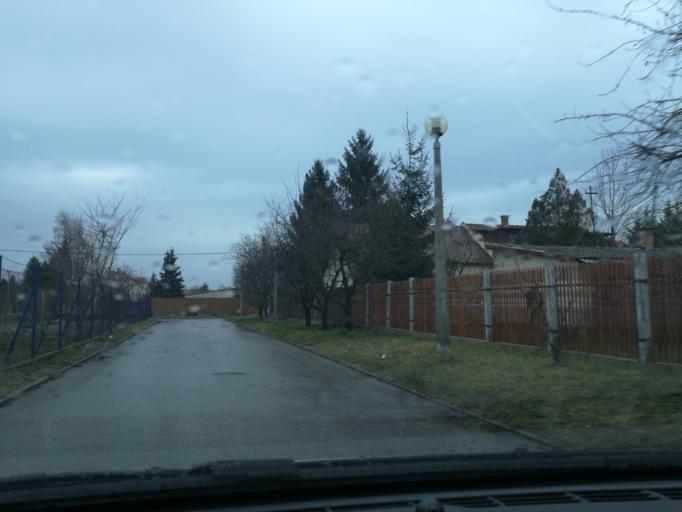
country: HU
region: Szabolcs-Szatmar-Bereg
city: Nyiregyhaza
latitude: 47.9684
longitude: 21.7015
